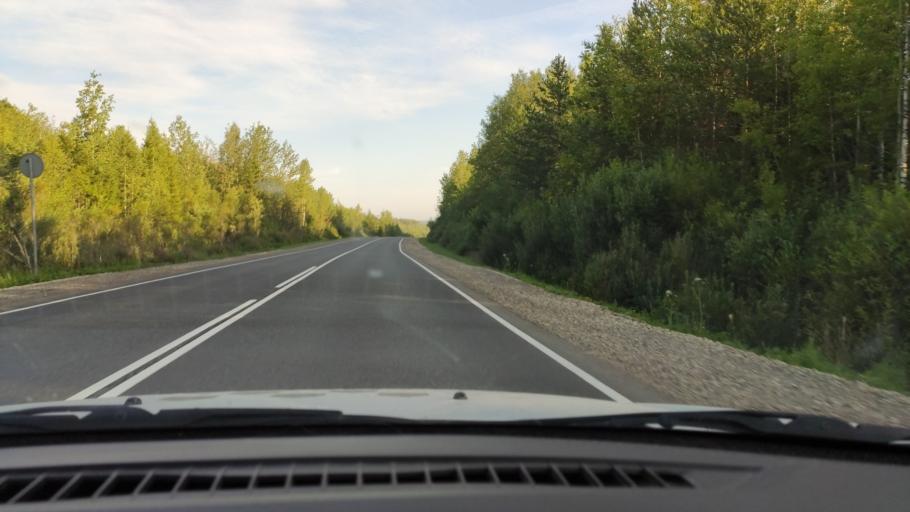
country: RU
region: Kirov
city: Omutninsk
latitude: 58.7082
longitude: 52.1011
